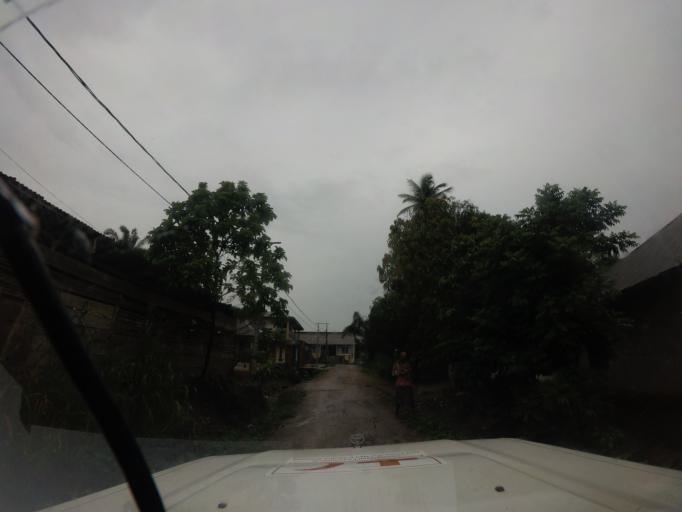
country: SL
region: Northern Province
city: Makeni
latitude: 8.8818
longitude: -12.0480
